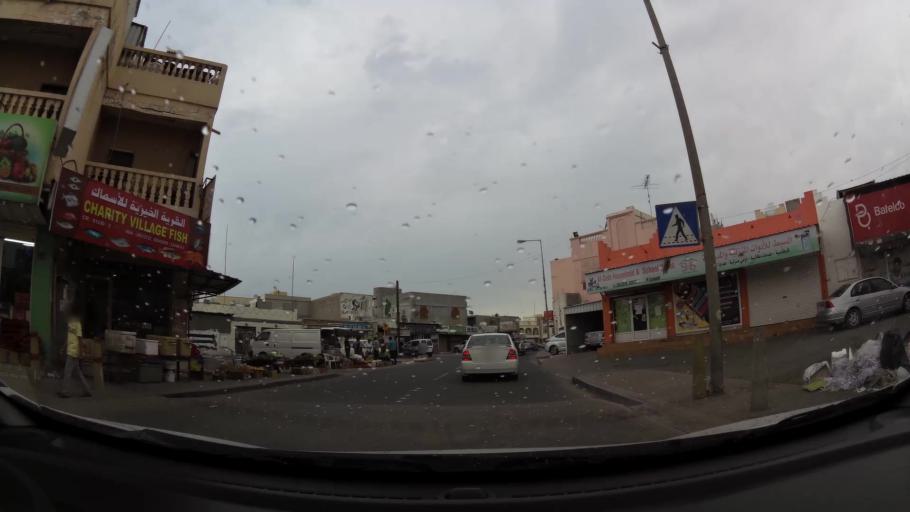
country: BH
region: Central Governorate
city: Madinat Hamad
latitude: 26.1153
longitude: 50.4818
